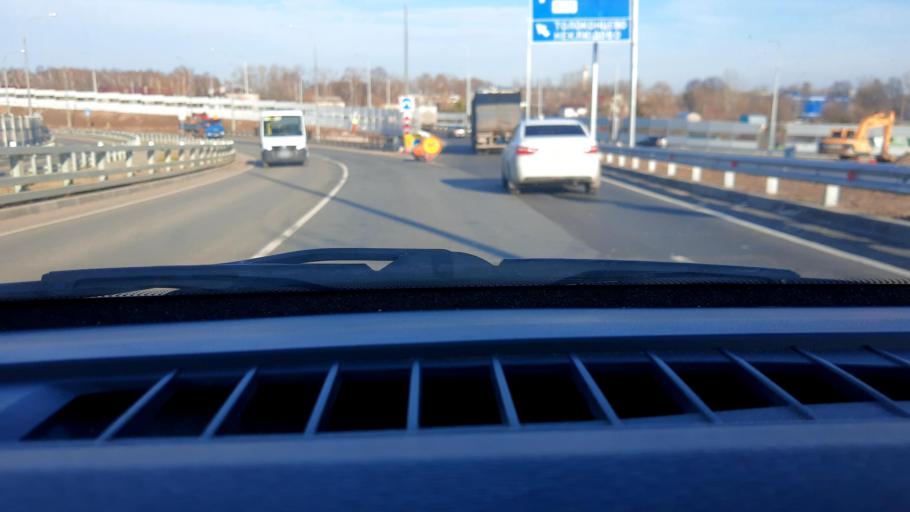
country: RU
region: Nizjnij Novgorod
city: Neklyudovo
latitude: 56.3990
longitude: 43.9908
